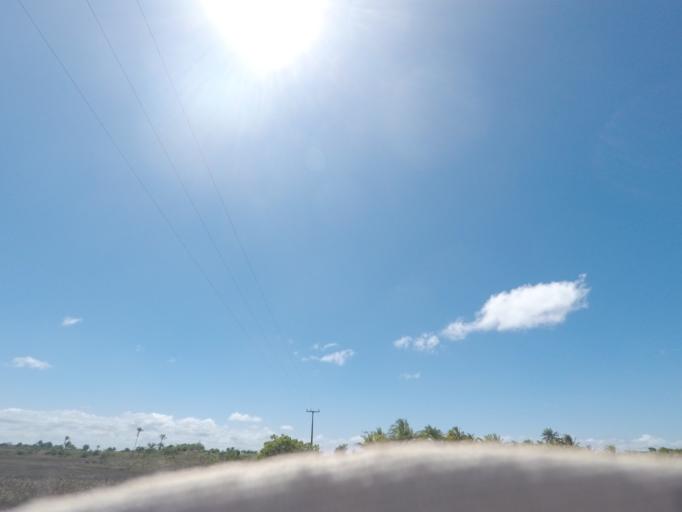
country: BR
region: Bahia
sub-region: Marau
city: Marau
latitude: -13.9680
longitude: -38.9422
